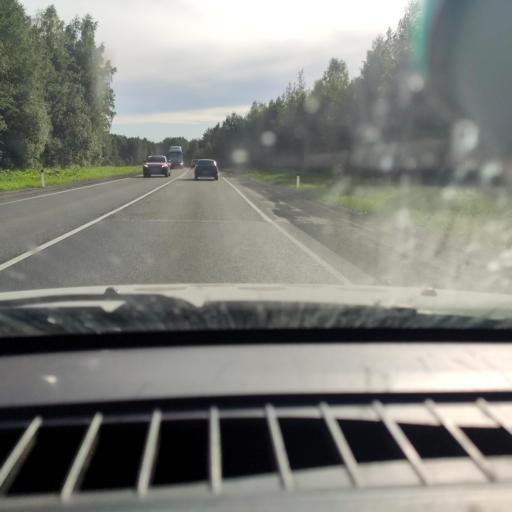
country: RU
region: Kirov
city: Vakhrushi
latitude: 58.6553
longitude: 49.8990
